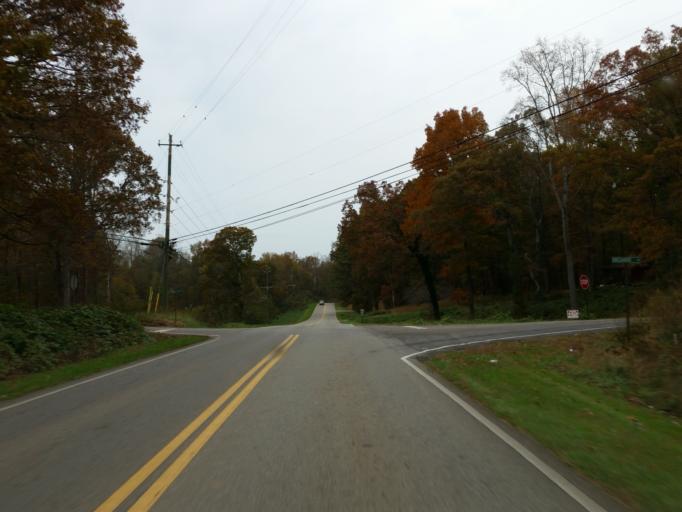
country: US
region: Georgia
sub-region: Pickens County
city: Jasper
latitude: 34.5048
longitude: -84.4388
